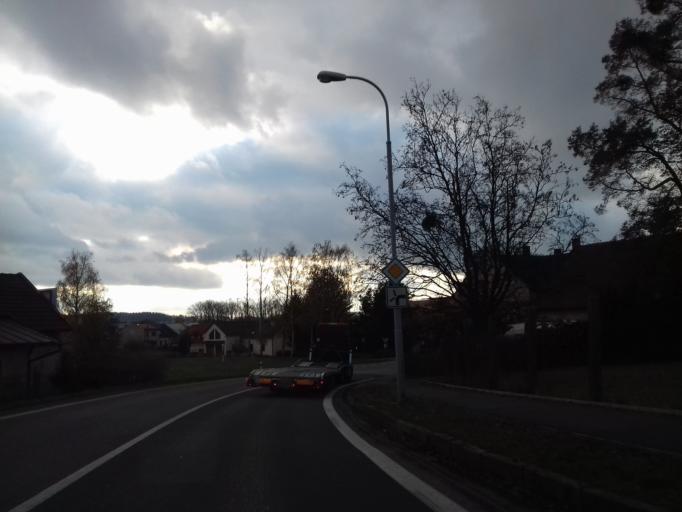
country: CZ
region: Pardubicky
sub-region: Okres Svitavy
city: Policka
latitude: 49.7188
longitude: 16.2848
